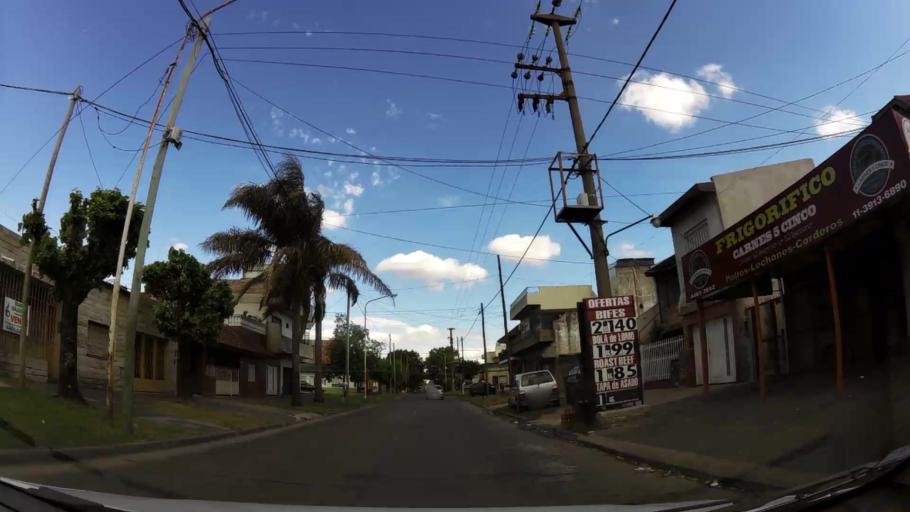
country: AR
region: Buenos Aires
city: San Justo
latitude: -34.6713
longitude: -58.5797
